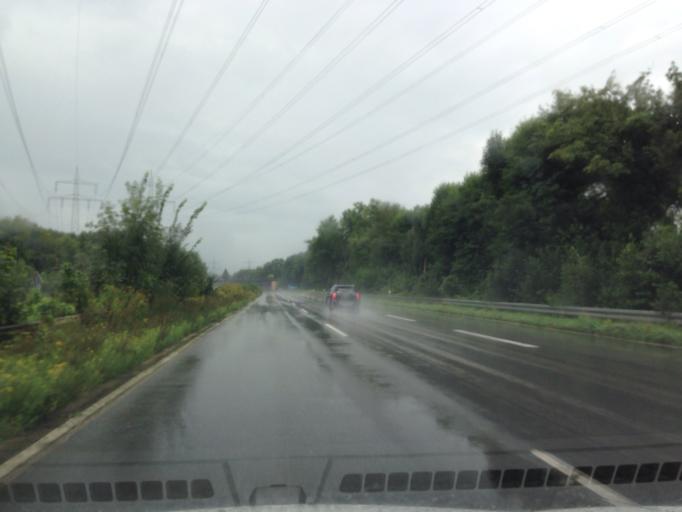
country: DE
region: North Rhine-Westphalia
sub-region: Regierungsbezirk Munster
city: Gladbeck
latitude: 51.5908
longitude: 7.0332
